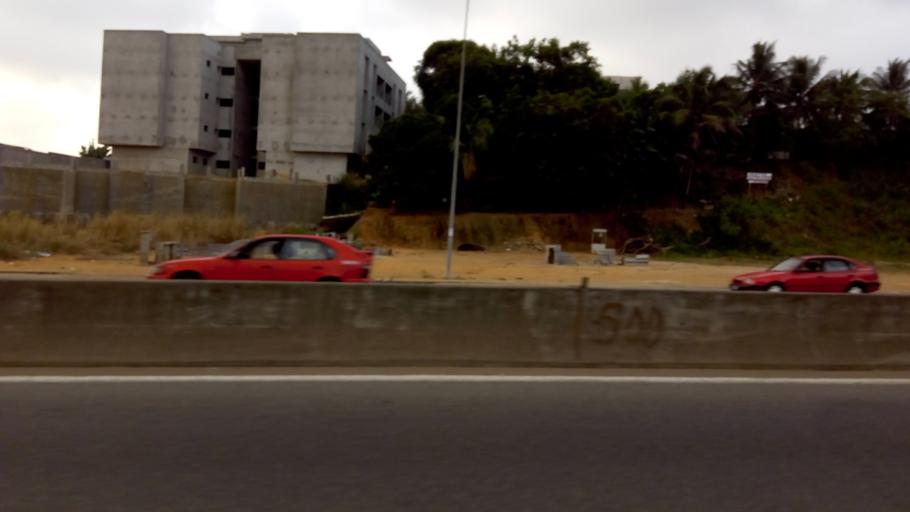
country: CI
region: Lagunes
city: Abidjan
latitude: 5.3523
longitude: -3.9814
